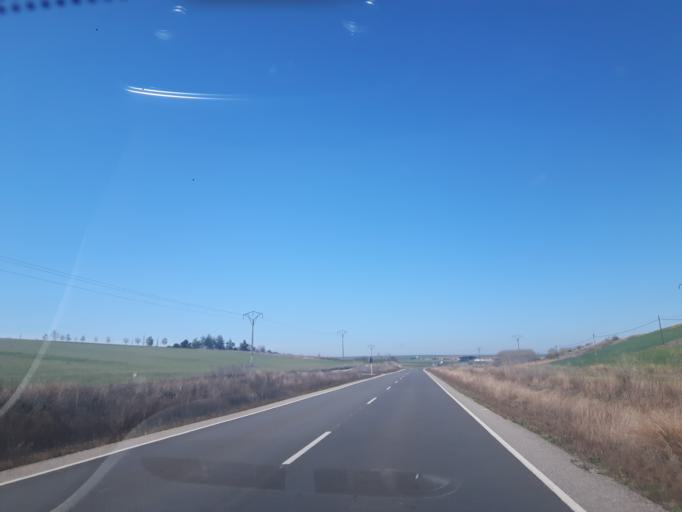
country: ES
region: Castille and Leon
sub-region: Provincia de Salamanca
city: Nava de Sotrobal
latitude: 40.8899
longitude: -5.2672
